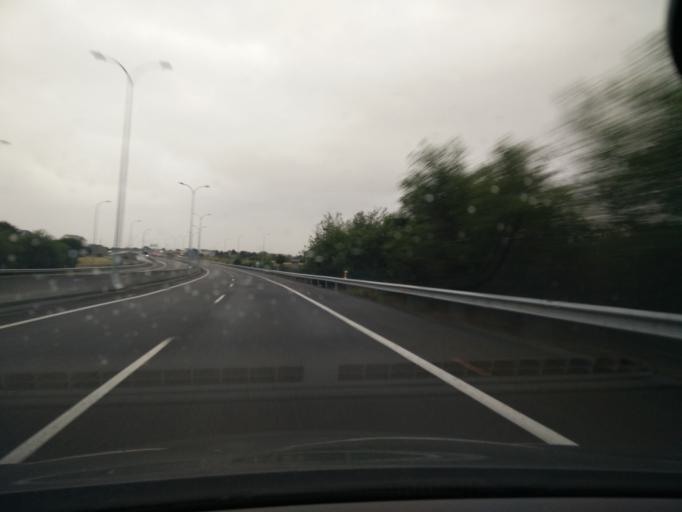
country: ES
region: Galicia
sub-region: Provincia de Lugo
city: Ribadeo
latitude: 43.5413
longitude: -7.0519
